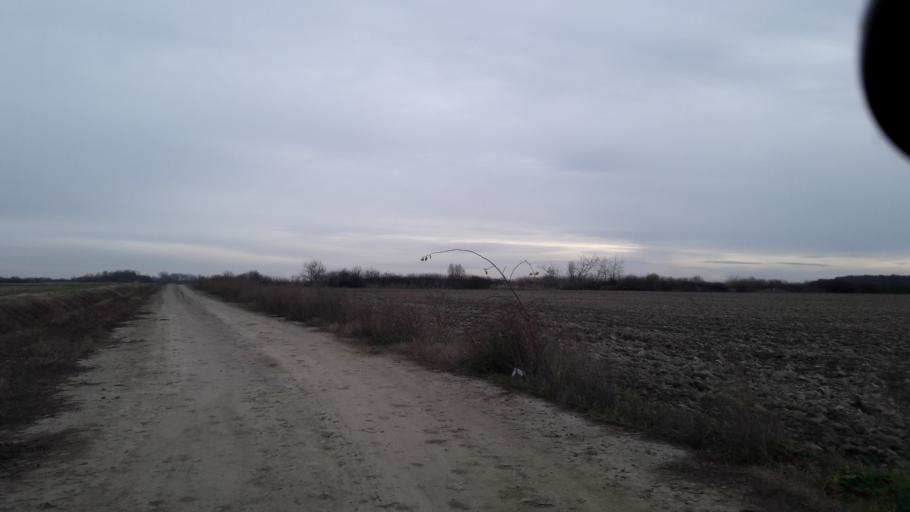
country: HR
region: Osjecko-Baranjska
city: Vladislavci
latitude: 45.4265
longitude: 18.5739
